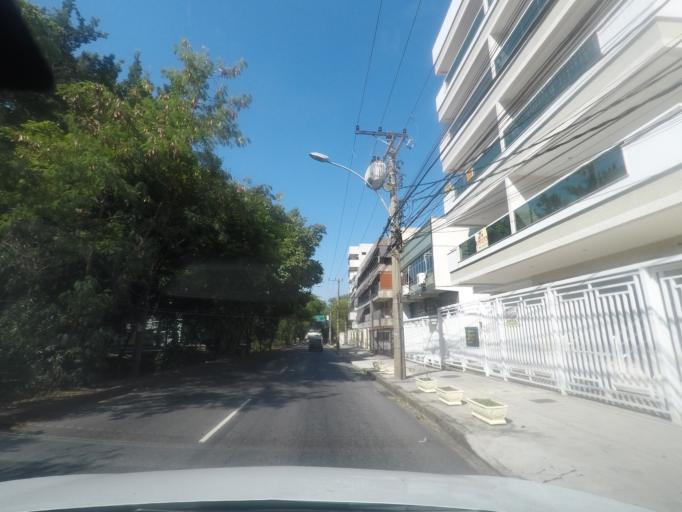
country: BR
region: Rio de Janeiro
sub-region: Sao Joao De Meriti
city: Sao Joao de Meriti
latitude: -22.8826
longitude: -43.3718
